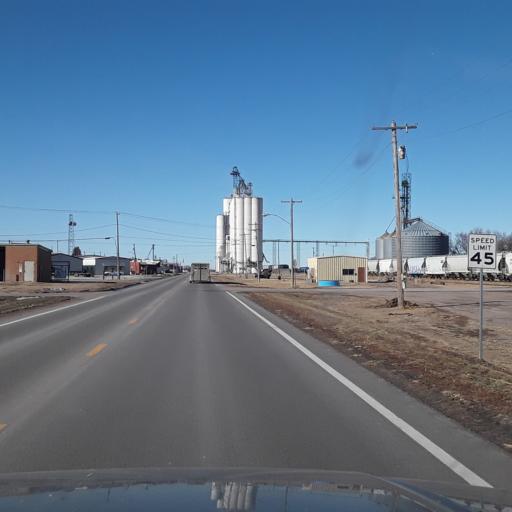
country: US
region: Nebraska
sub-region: Gosper County
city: Elwood
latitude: 40.5268
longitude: -99.6303
